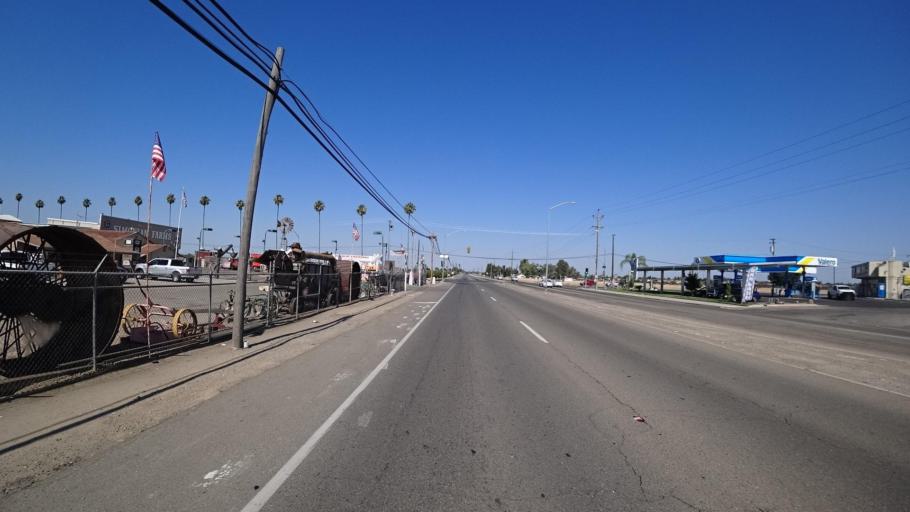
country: US
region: California
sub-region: Fresno County
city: Sunnyside
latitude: 36.7074
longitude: -119.6990
